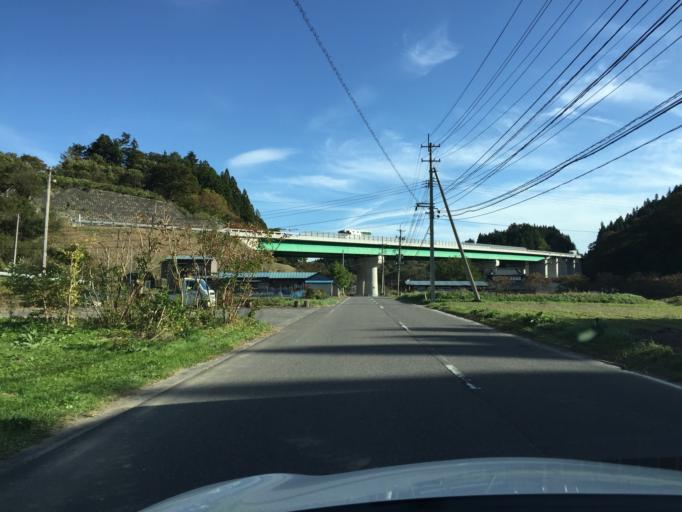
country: JP
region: Fukushima
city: Funehikimachi-funehiki
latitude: 37.3149
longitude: 140.6089
